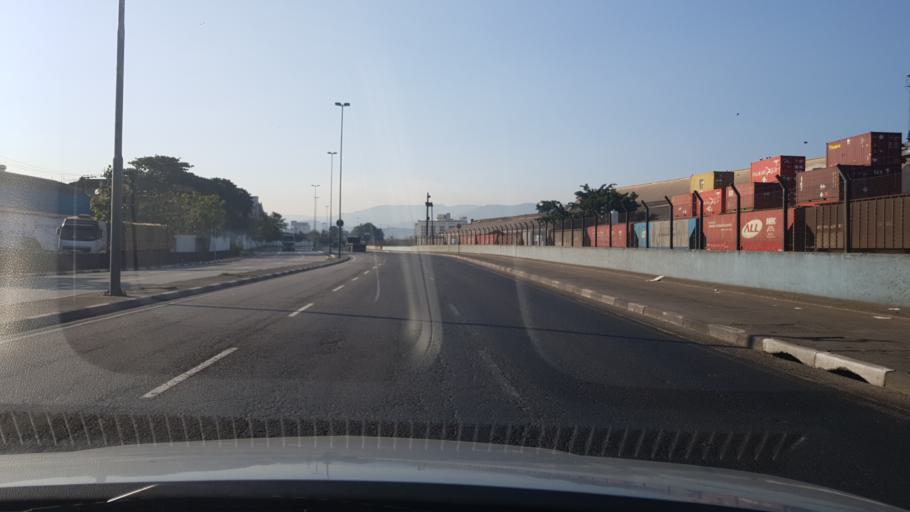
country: BR
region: Sao Paulo
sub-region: Santos
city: Santos
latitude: -23.9471
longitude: -46.3175
